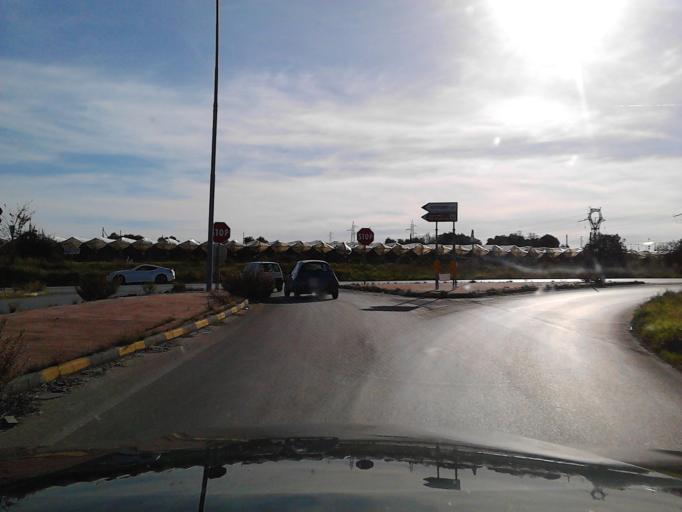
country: IT
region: Apulia
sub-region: Provincia di Bari
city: Rutigliano
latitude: 41.0078
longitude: 16.9891
